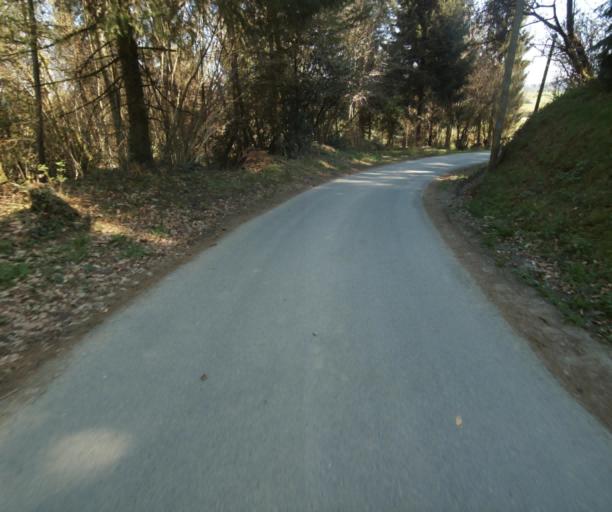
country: FR
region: Limousin
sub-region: Departement de la Correze
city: Saint-Mexant
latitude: 45.2964
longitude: 1.6075
